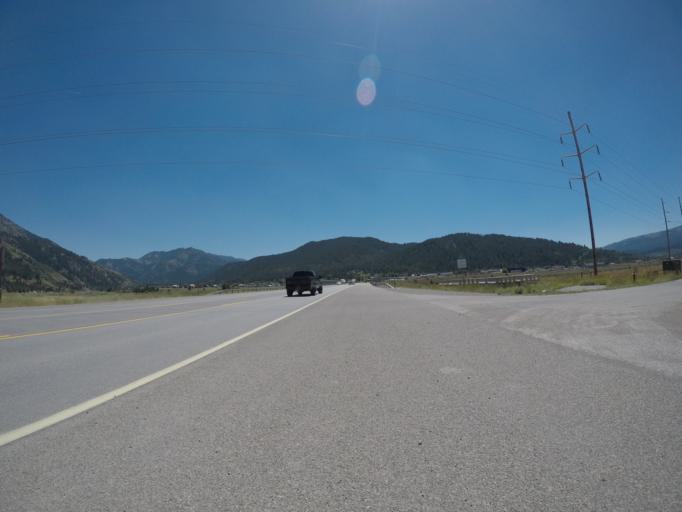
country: US
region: Wyoming
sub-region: Teton County
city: Hoback
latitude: 43.1690
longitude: -111.0180
